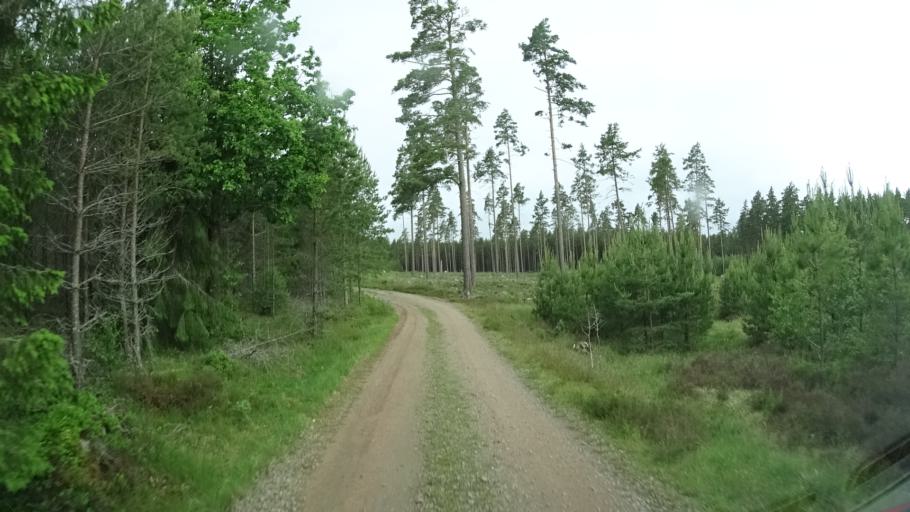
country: SE
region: Kalmar
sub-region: Vimmerby Kommun
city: Sodra Vi
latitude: 57.7153
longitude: 15.7797
